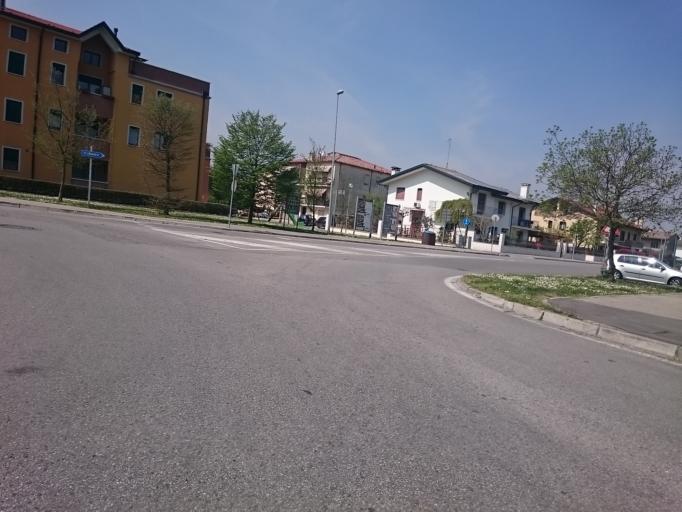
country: IT
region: Veneto
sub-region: Provincia di Padova
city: Tencarola
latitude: 45.3982
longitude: 11.8060
